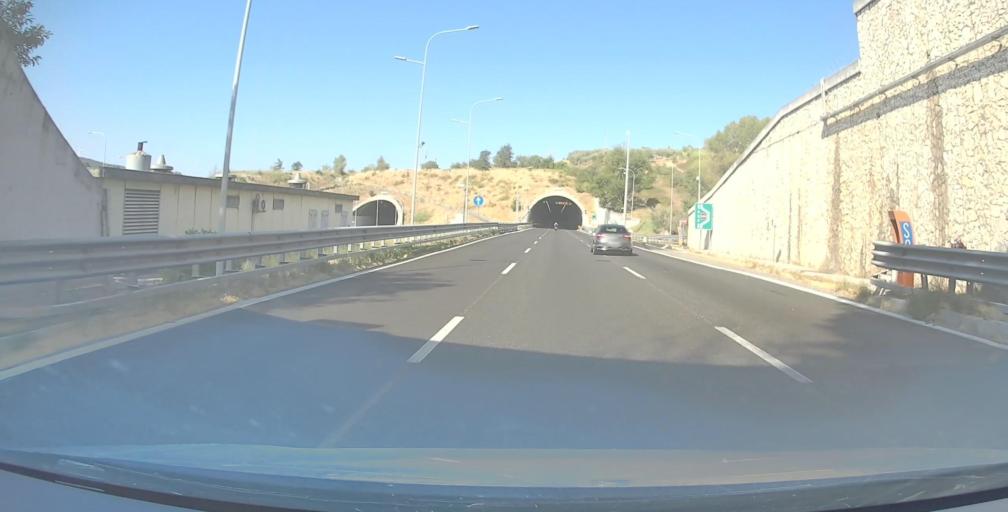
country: IT
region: Campania
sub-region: Provincia di Salerno
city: Contursi Terme
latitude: 40.6279
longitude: 15.2078
